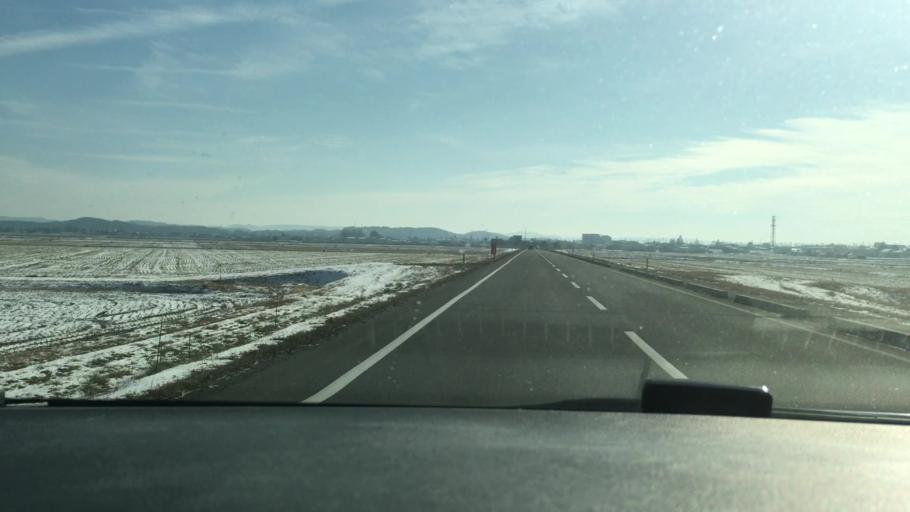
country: JP
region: Iwate
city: Ichinoseki
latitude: 38.7817
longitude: 141.1239
